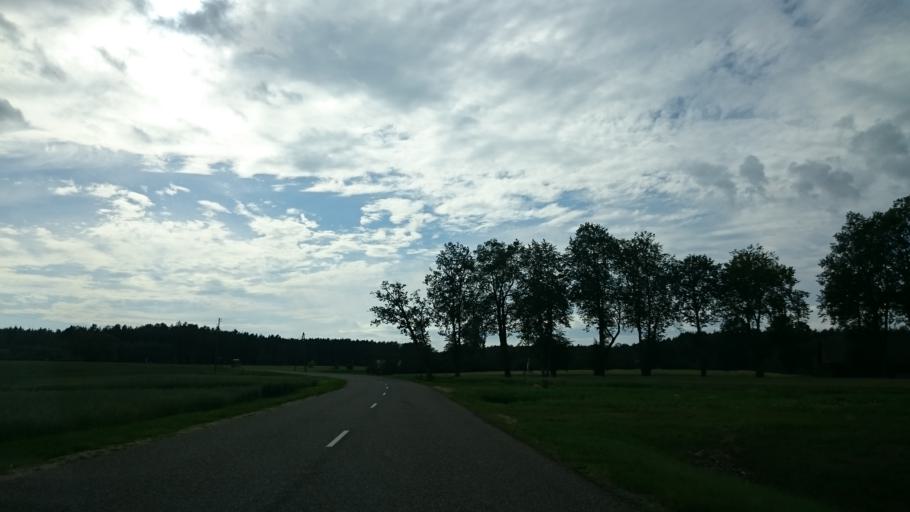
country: LV
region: Saulkrastu
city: Saulkrasti
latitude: 57.2505
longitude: 24.5075
